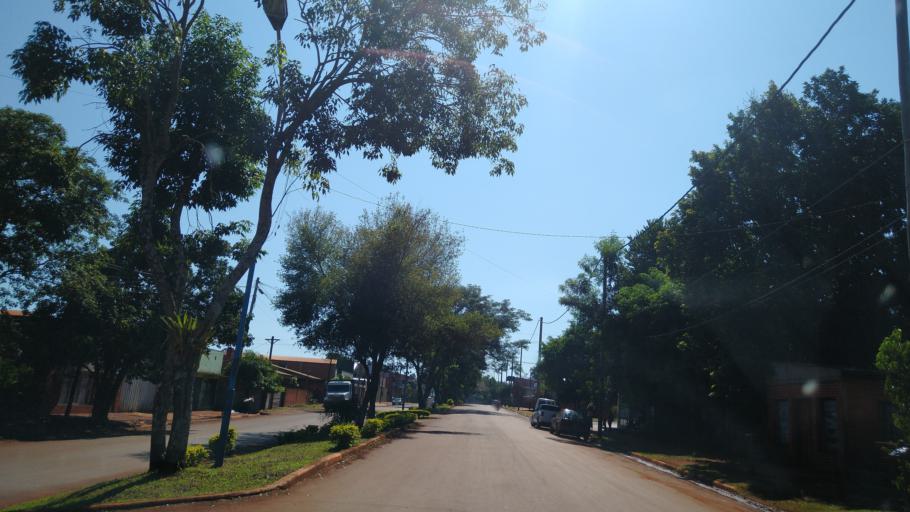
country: AR
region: Misiones
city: Puerto Libertad
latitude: -25.9752
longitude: -54.5693
